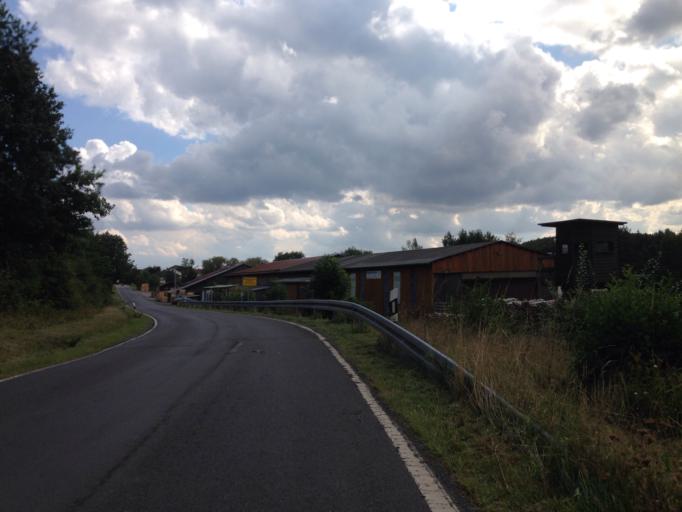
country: DE
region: Hesse
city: Mengerskirchen
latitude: 50.5426
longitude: 8.1589
